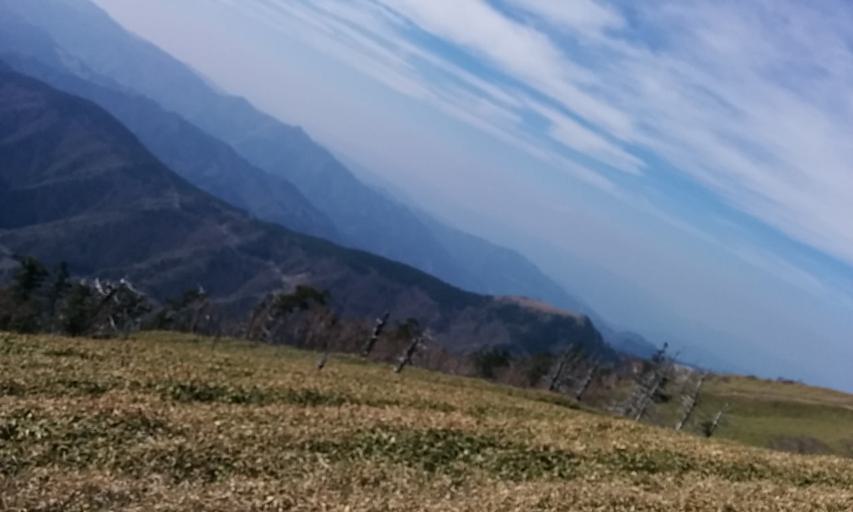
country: JP
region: Tokushima
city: Wakimachi
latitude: 33.8535
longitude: 134.0941
